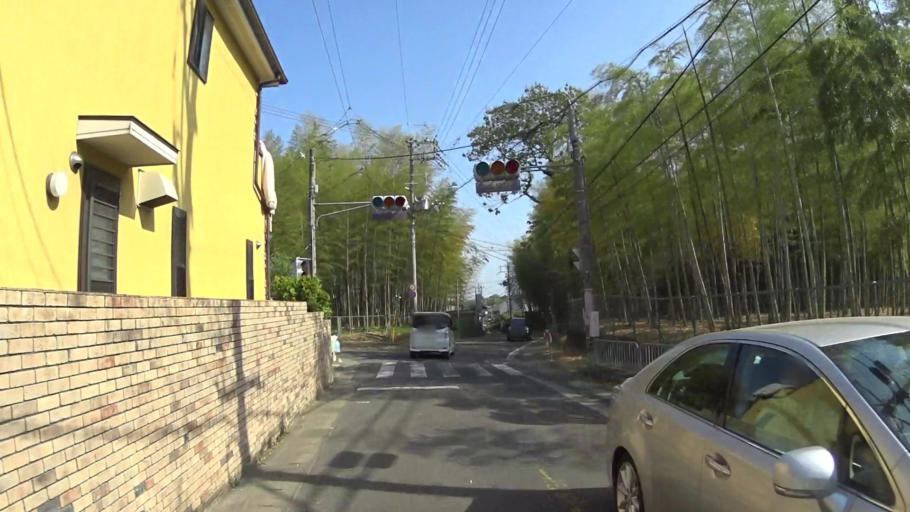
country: JP
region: Kyoto
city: Muko
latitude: 34.9520
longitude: 135.6764
